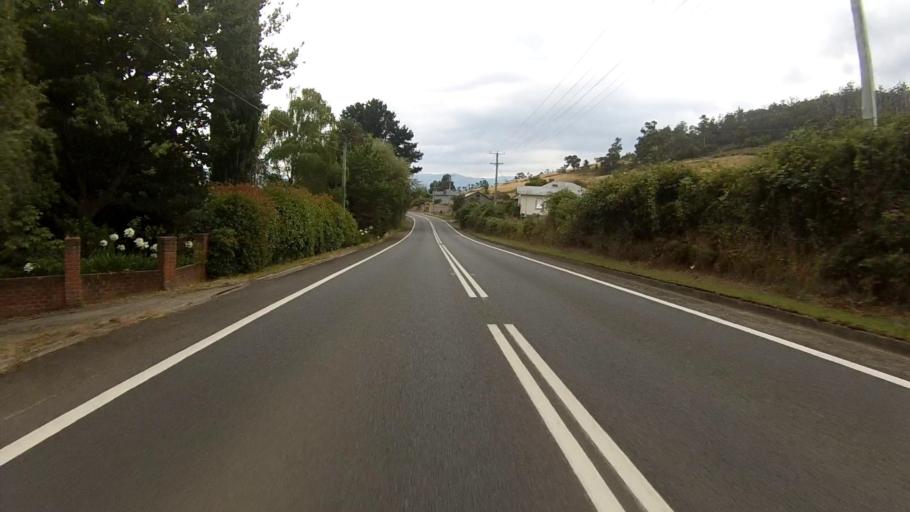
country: AU
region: Tasmania
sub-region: Huon Valley
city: Huonville
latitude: -43.0499
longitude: 147.0503
